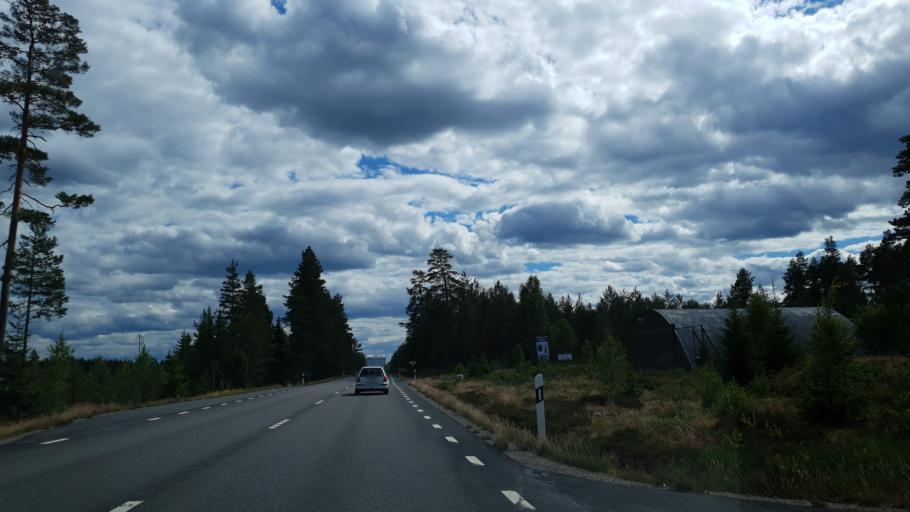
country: SE
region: Kronoberg
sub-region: Lessebo Kommun
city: Lessebo
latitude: 56.8030
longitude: 15.4125
